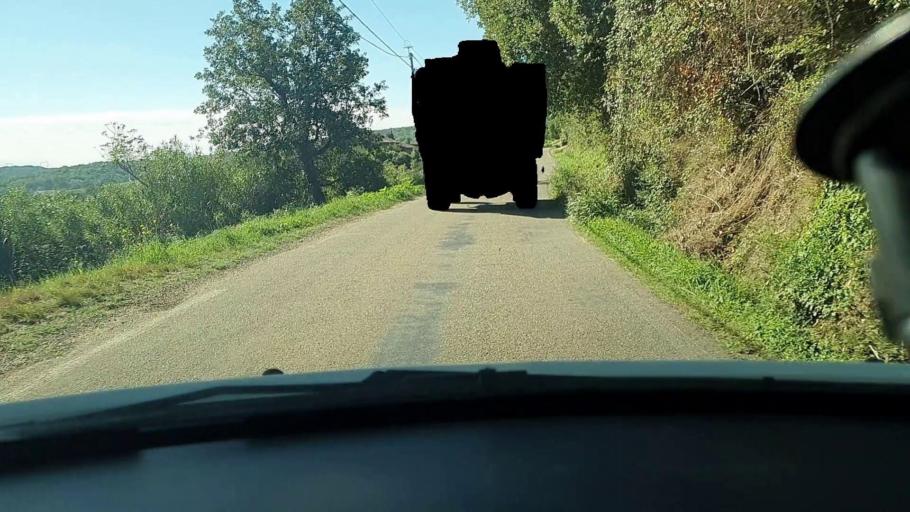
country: FR
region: Languedoc-Roussillon
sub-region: Departement du Gard
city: Saint-Julien-de-Peyrolas
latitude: 44.2728
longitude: 4.5720
